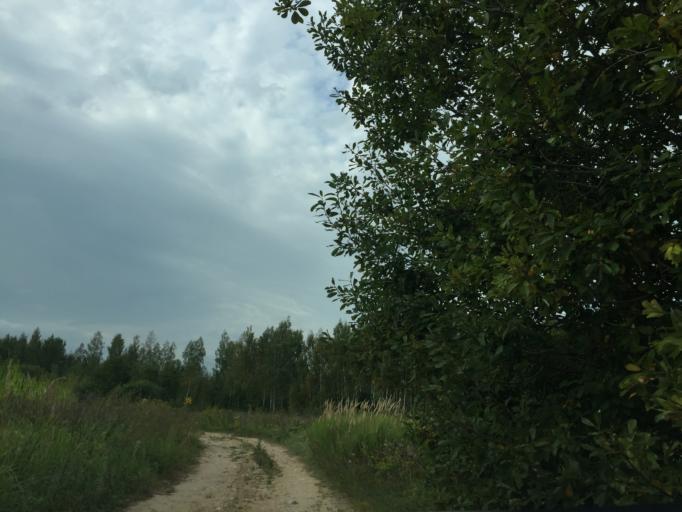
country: LV
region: Baldone
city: Baldone
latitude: 56.7649
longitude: 24.4655
